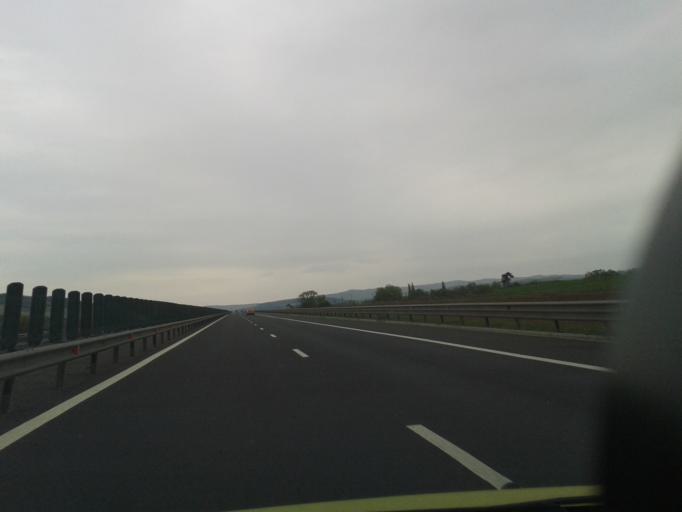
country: RO
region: Sibiu
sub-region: Oras Miercurea Sibiului
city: Miercurea Sibiului
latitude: 45.8986
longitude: 23.7755
